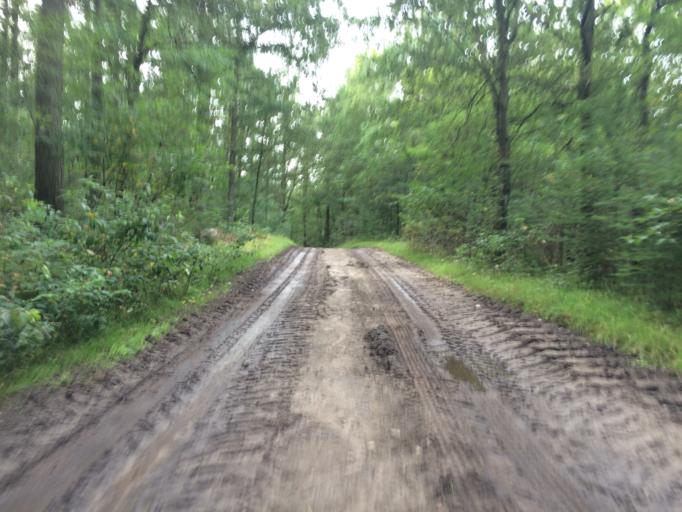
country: DK
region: Central Jutland
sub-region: Holstebro Kommune
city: Ulfborg
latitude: 56.2256
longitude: 8.4035
